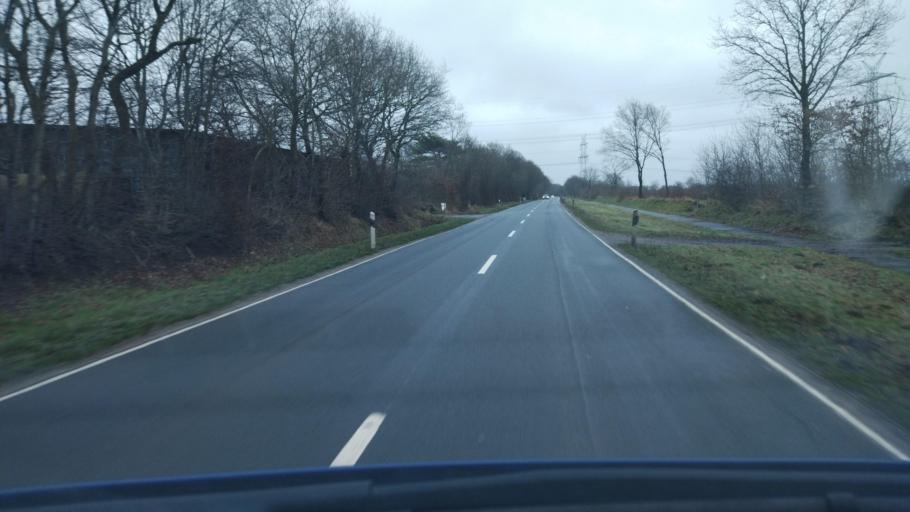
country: DE
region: Schleswig-Holstein
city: Gross Rheide
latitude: 54.4464
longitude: 9.4160
